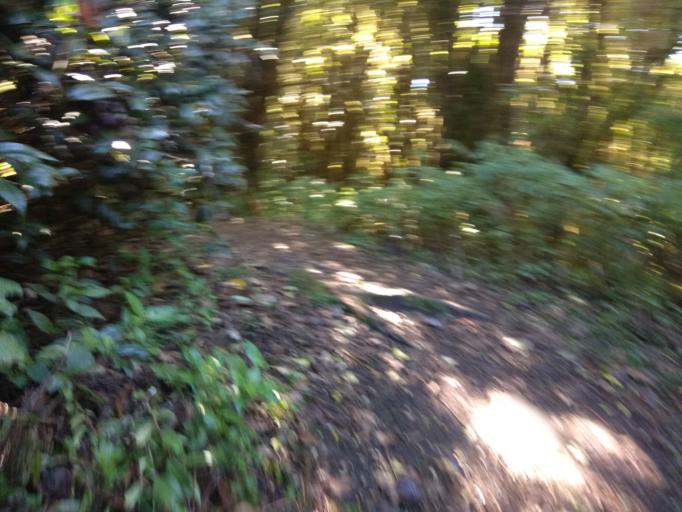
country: CR
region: Heredia
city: Santo Domingo
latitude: 10.1318
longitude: -84.1196
